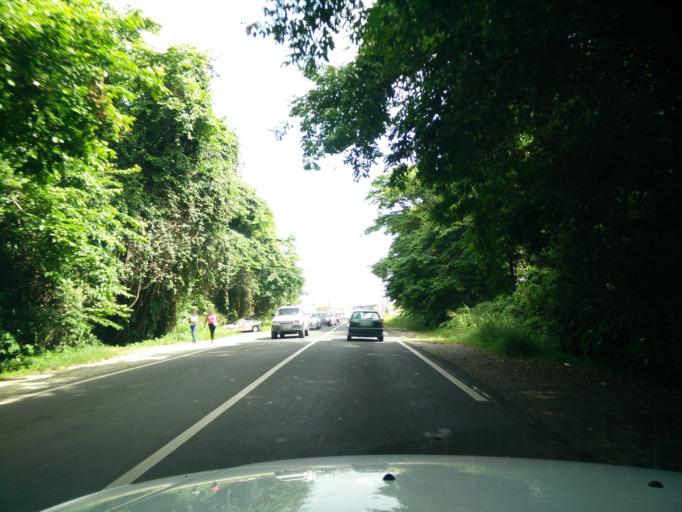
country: GP
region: Guadeloupe
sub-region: Guadeloupe
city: Baie-Mahault
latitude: 16.2495
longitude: -61.5710
